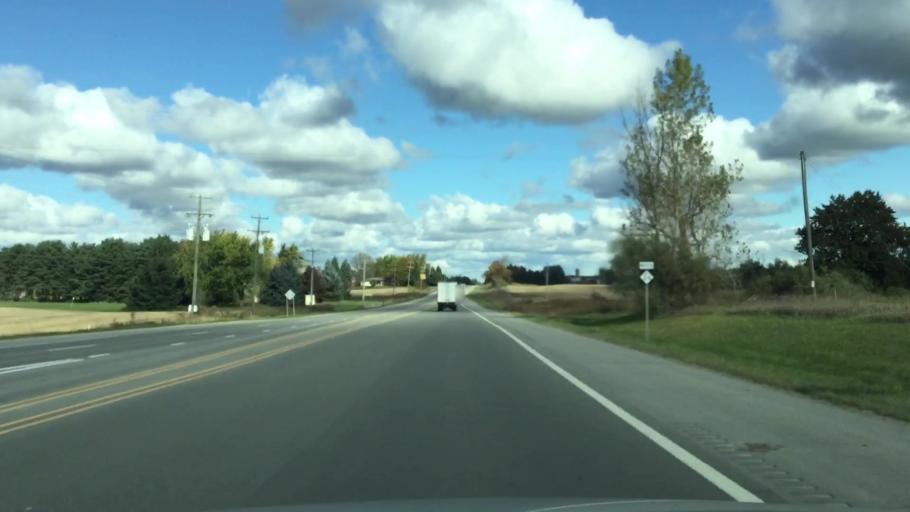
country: US
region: Michigan
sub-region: Oakland County
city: Oxford
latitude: 42.8983
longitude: -83.3116
